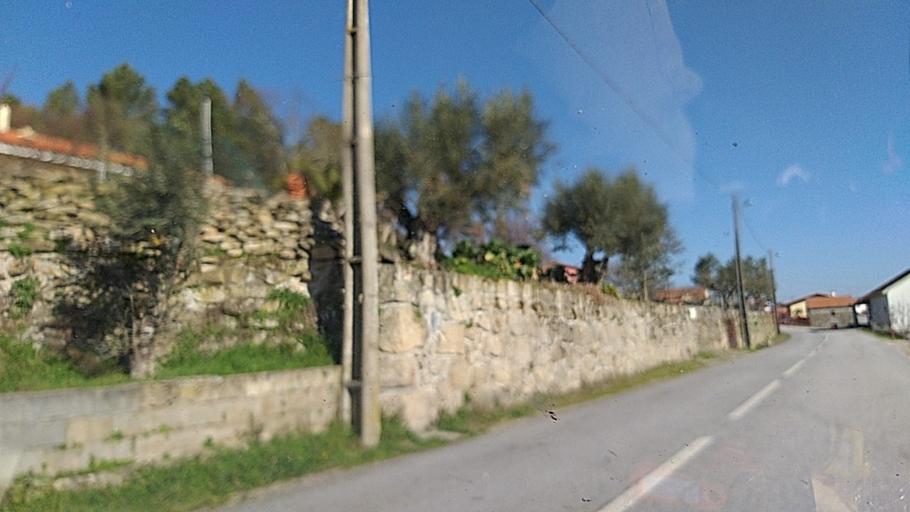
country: PT
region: Guarda
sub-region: Celorico da Beira
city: Celorico da Beira
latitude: 40.6514
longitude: -7.4656
